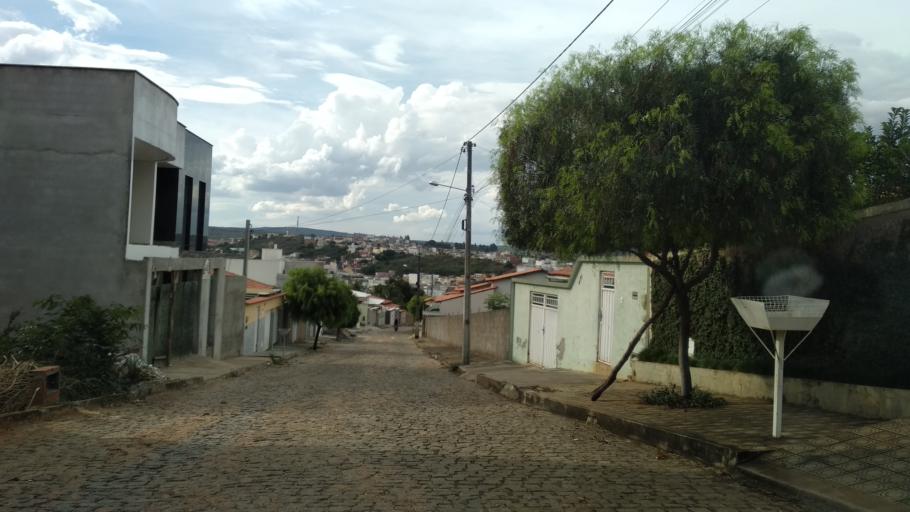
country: BR
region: Bahia
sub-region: Caetite
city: Caetite
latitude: -14.0724
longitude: -42.4790
